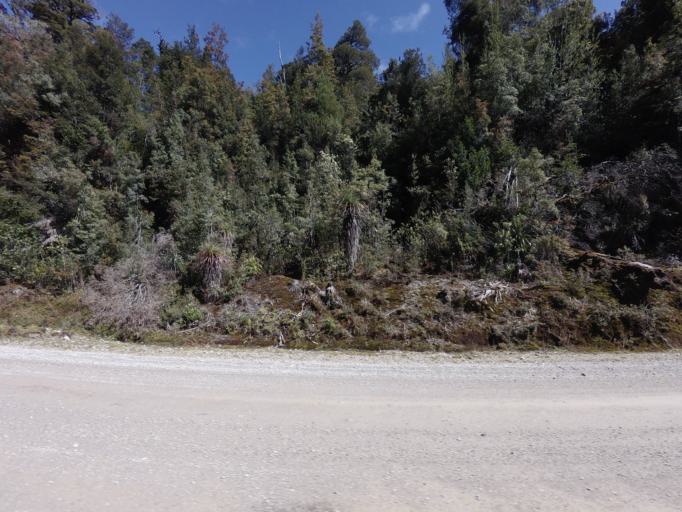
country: AU
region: Tasmania
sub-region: Huon Valley
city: Geeveston
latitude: -42.8336
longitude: 146.3828
